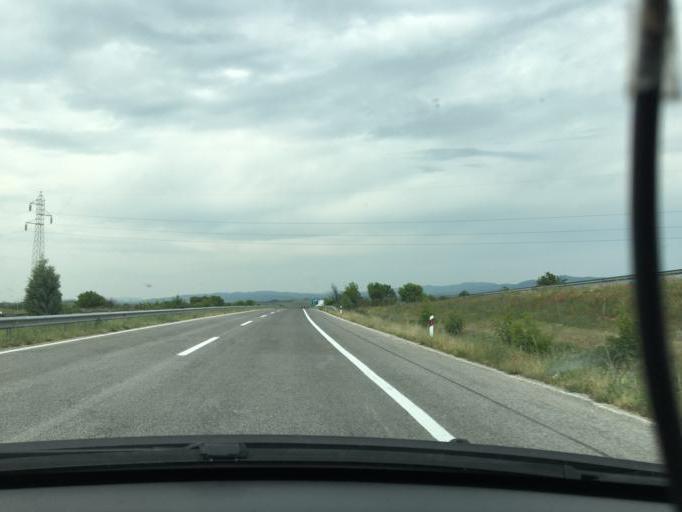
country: MK
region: Negotino
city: Negotino
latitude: 41.4793
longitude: 22.1076
